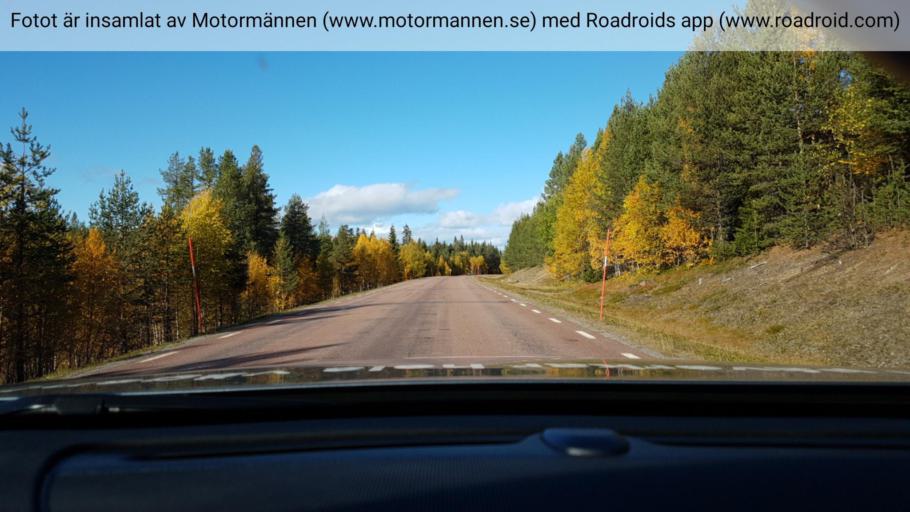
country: SE
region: Norrbotten
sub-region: Arjeplogs Kommun
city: Arjeplog
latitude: 66.0116
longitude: 18.0908
